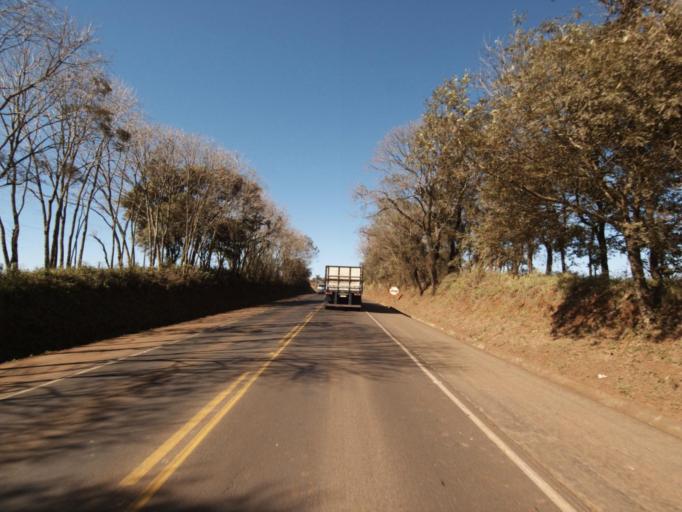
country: BR
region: Santa Catarina
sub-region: Chapeco
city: Chapeco
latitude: -26.8674
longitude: -52.9651
